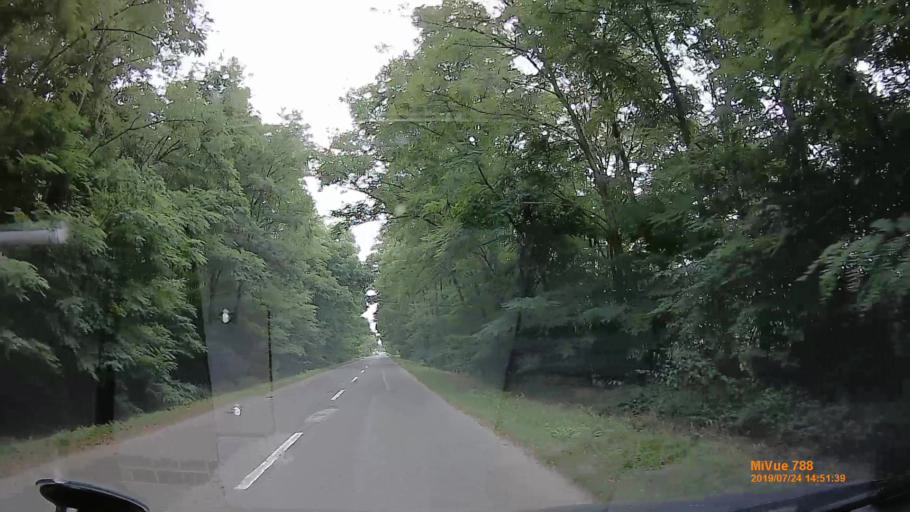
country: HU
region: Szabolcs-Szatmar-Bereg
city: Aranyosapati
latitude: 48.2703
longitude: 22.2858
